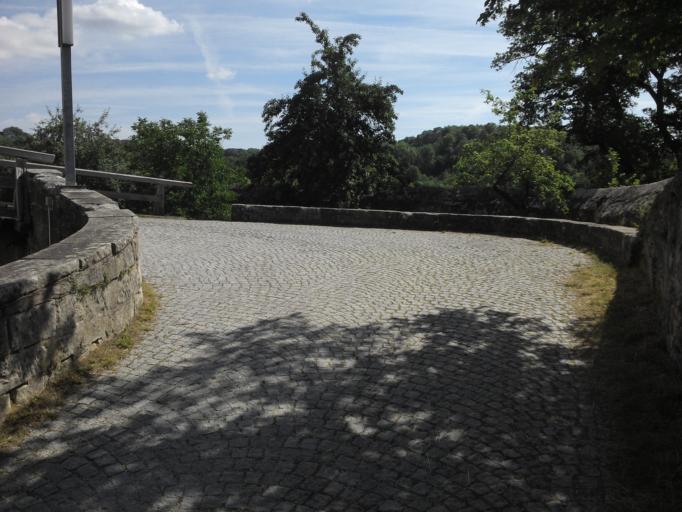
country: DE
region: Baden-Wuerttemberg
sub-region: Regierungsbezirk Stuttgart
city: Huttlingen
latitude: 48.8964
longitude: 10.0767
